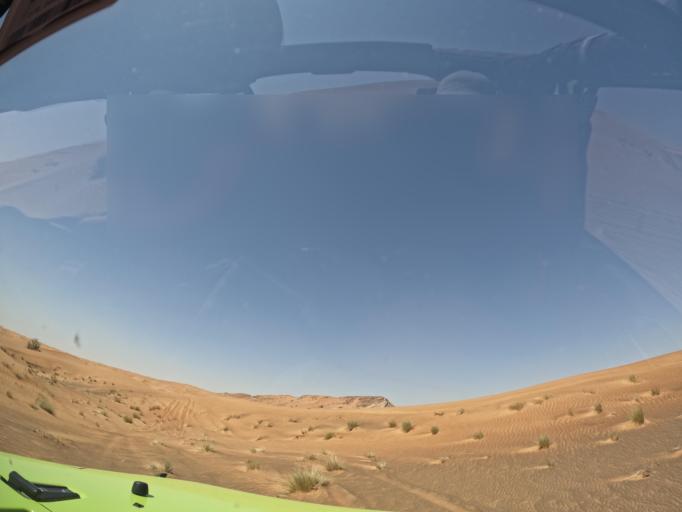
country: AE
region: Ash Shariqah
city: Adh Dhayd
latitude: 25.0187
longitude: 55.7399
